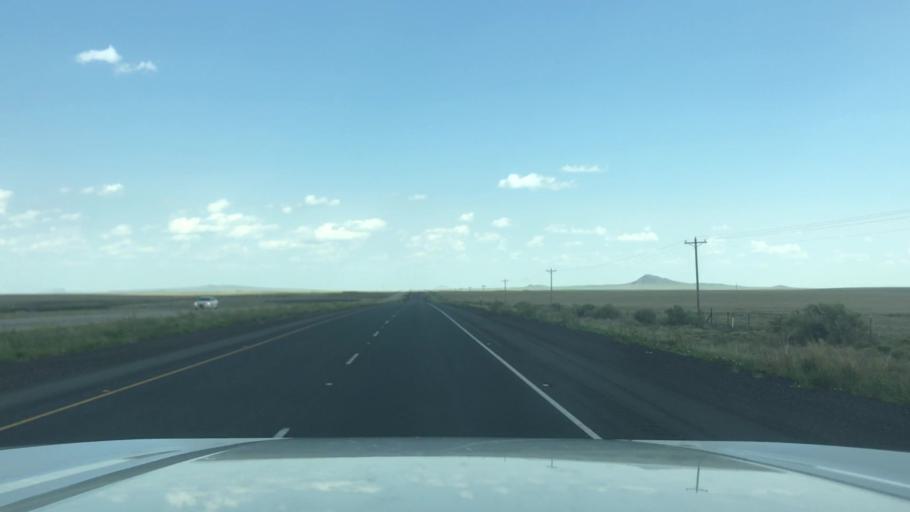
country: US
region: New Mexico
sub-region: Union County
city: Clayton
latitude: 36.6296
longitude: -103.7111
